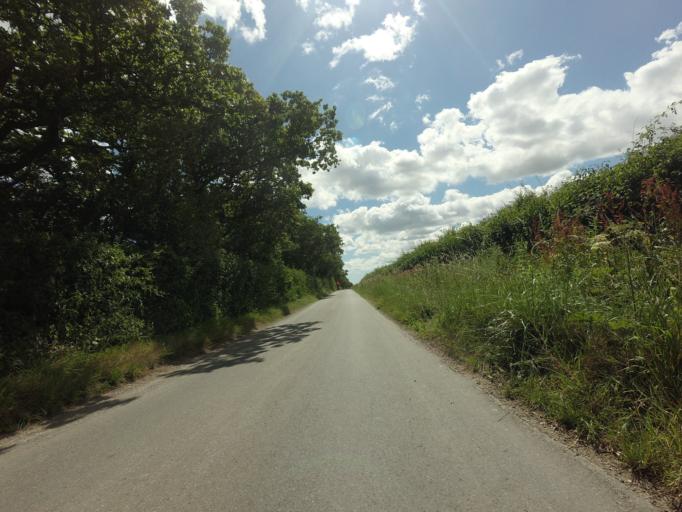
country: GB
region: England
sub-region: East Sussex
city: Ringmer
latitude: 50.8598
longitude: 0.1486
